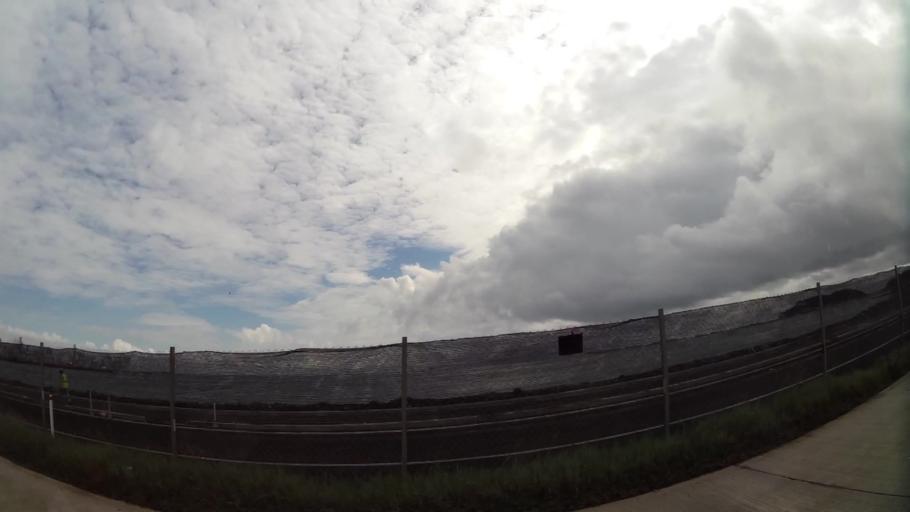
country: PA
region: Panama
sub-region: Distrito de Panama
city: Ancon
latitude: 8.9304
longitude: -79.5438
